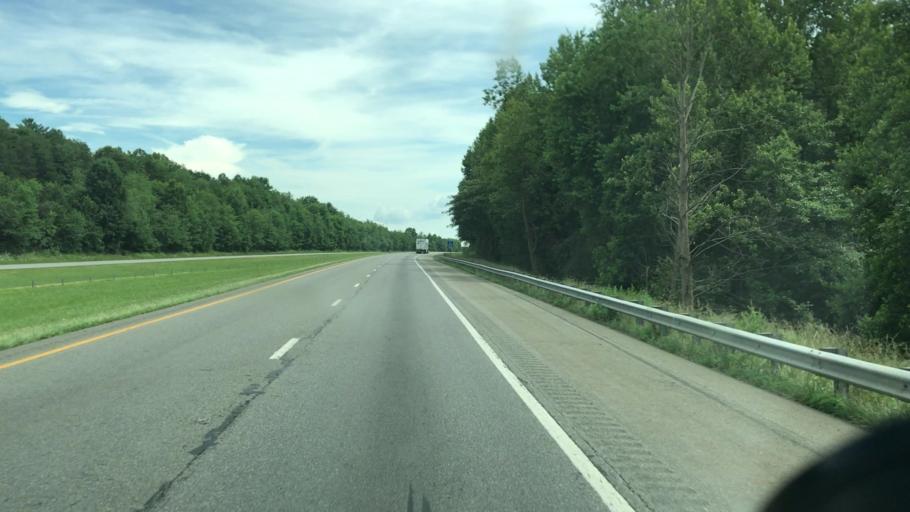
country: US
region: North Carolina
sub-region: Surry County
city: Dobson
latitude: 36.3328
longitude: -80.7942
